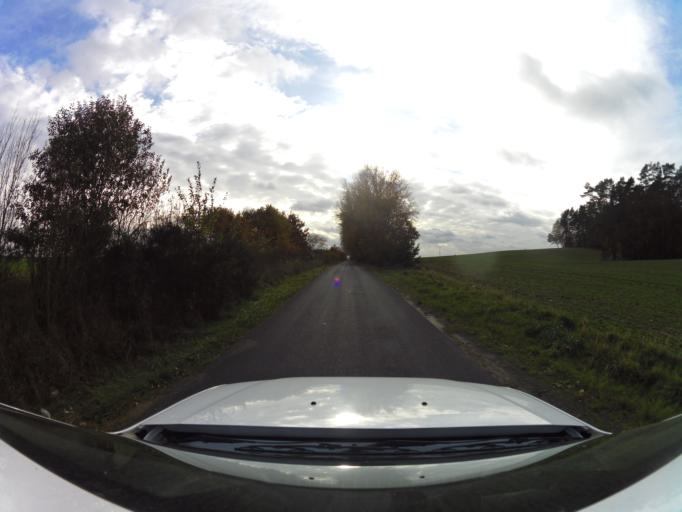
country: PL
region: West Pomeranian Voivodeship
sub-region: Powiat gryficki
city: Gryfice
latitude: 53.9028
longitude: 15.1330
